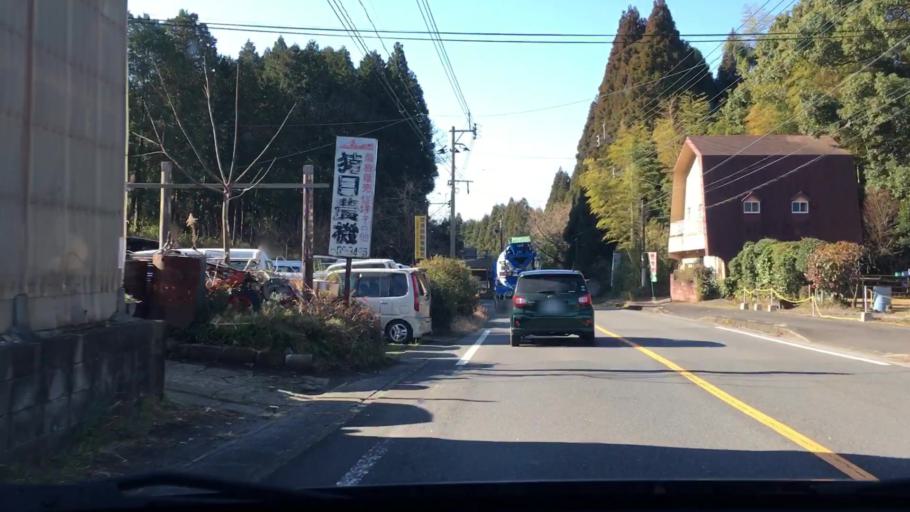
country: JP
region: Kagoshima
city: Kajiki
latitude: 31.7769
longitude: 130.7018
